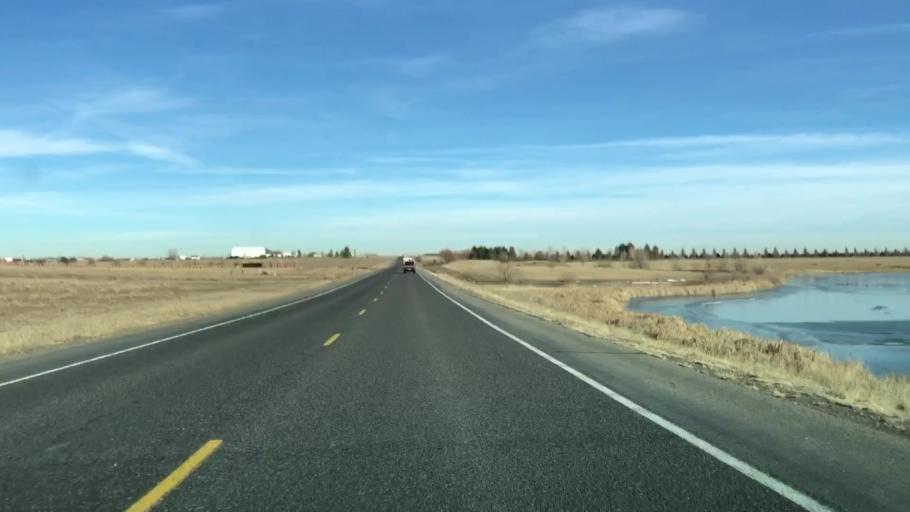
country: US
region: Colorado
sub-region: Weld County
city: Windsor
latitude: 40.4245
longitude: -104.9447
